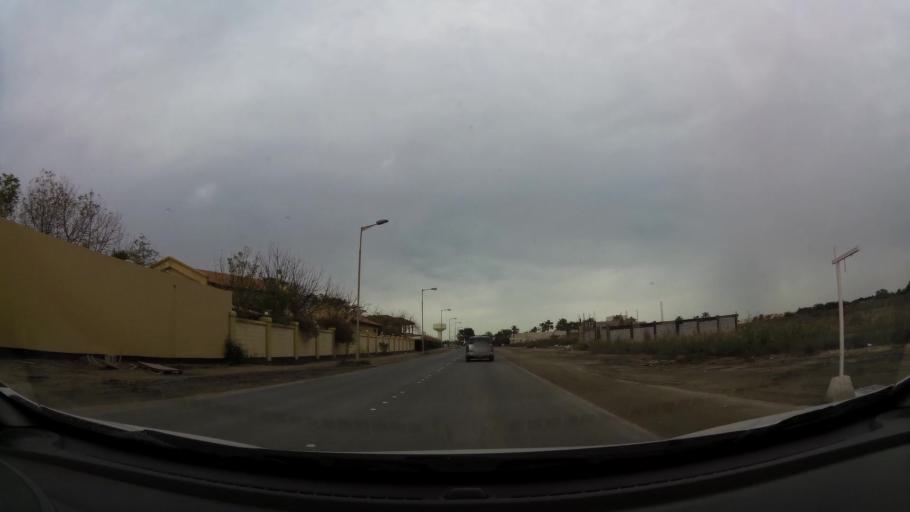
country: BH
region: Central Governorate
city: Madinat Hamad
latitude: 26.1353
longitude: 50.4645
